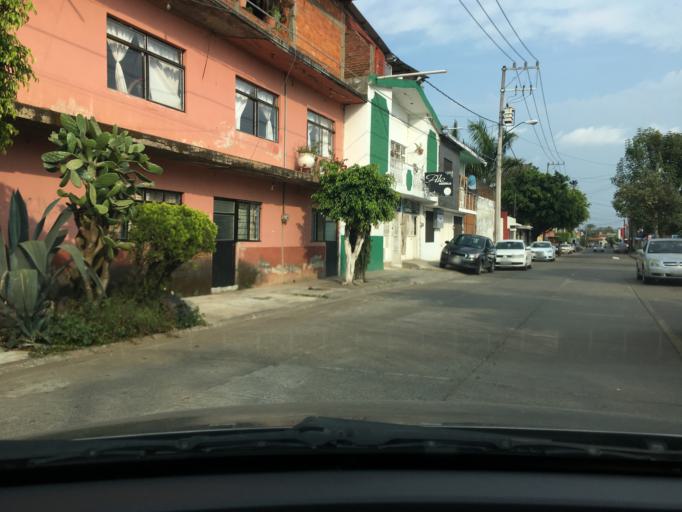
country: MX
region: Michoacan
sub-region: Uruapan
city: Uruapan
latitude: 19.4115
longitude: -102.0495
